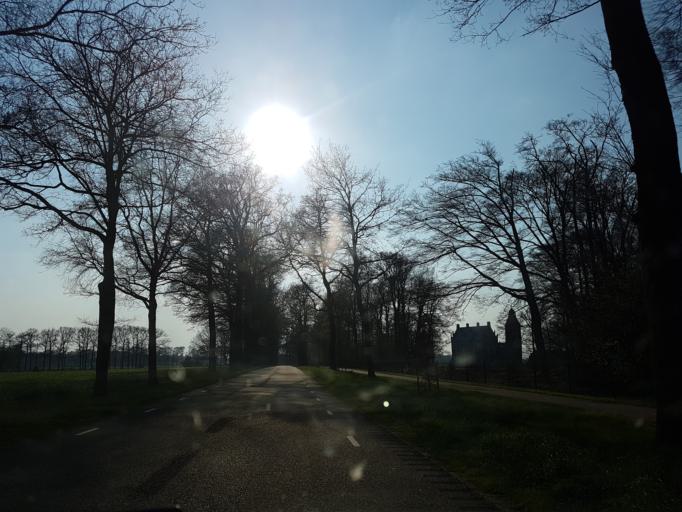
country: NL
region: Overijssel
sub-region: Gemeente Dalfsen
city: Dalfsen
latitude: 52.4978
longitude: 6.2943
